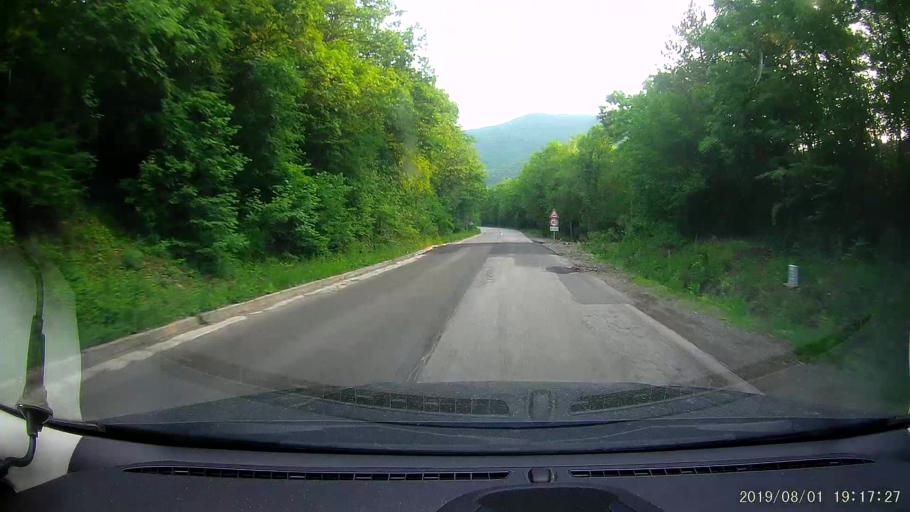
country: BG
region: Shumen
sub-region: Obshtina Smyadovo
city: Smyadovo
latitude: 42.9233
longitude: 26.9426
